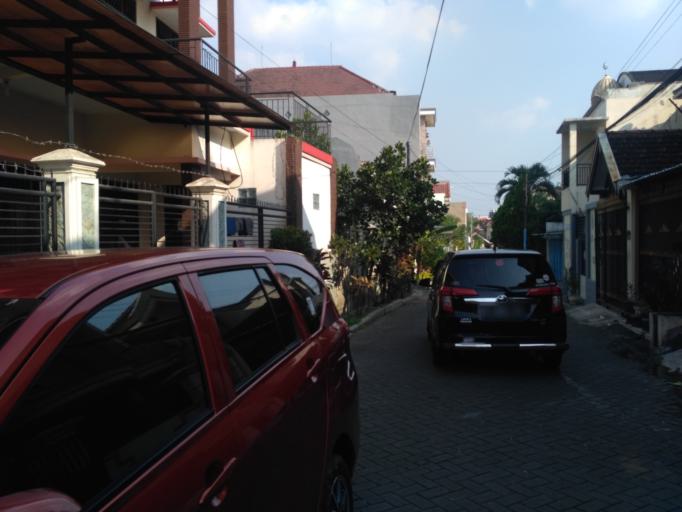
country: ID
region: East Java
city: Malang
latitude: -7.9557
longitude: 112.6098
